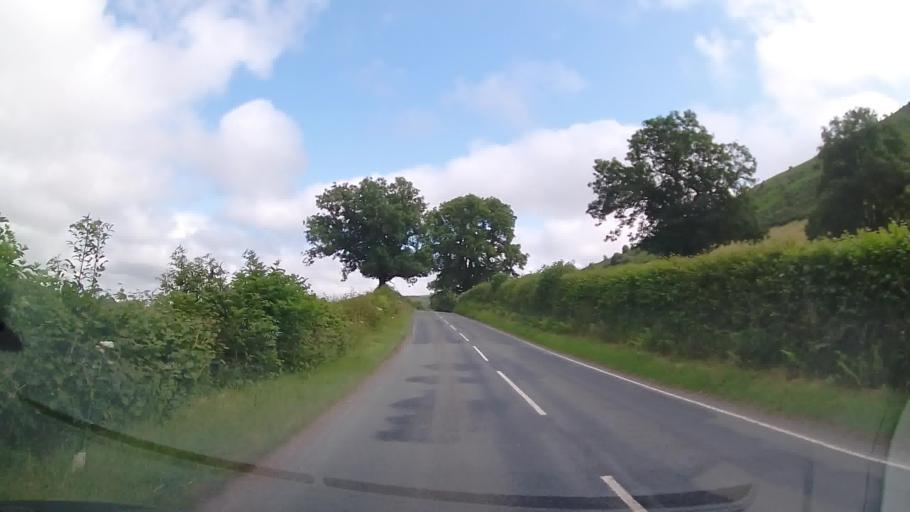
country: GB
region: Wales
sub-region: Sir Powys
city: Llangynog
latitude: 52.8196
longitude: -3.3771
